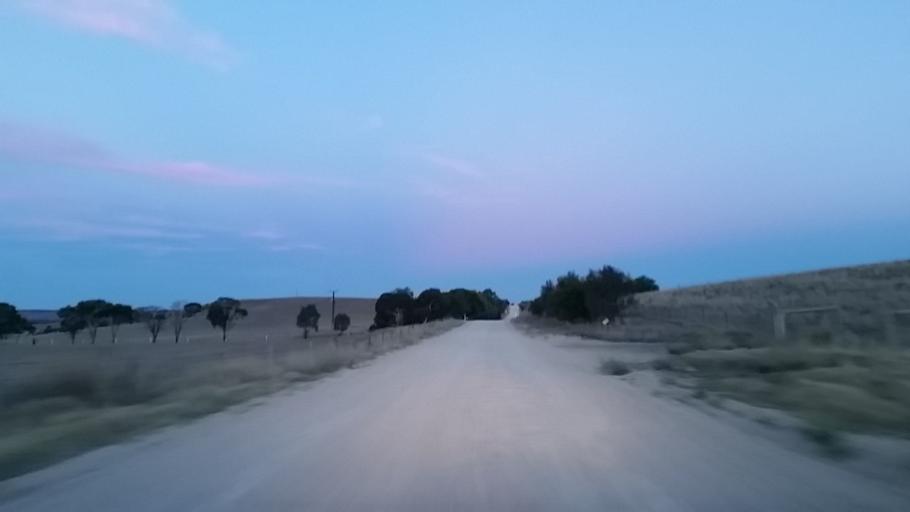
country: AU
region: South Australia
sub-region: Mount Barker
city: Callington
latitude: -35.1054
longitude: 139.0176
